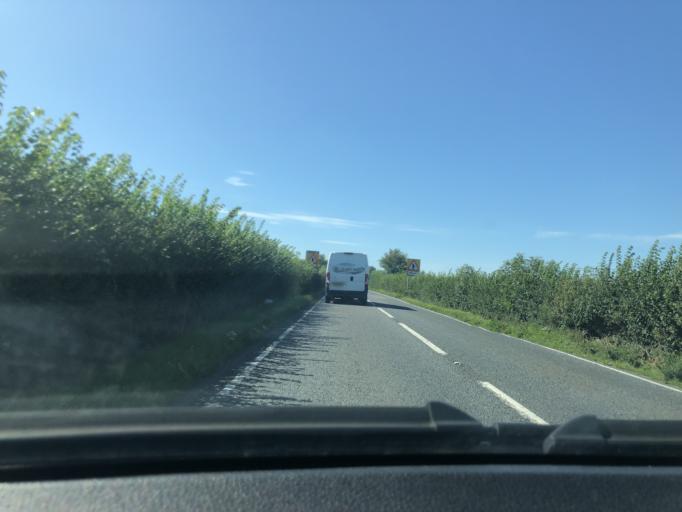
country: GB
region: England
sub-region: Somerset
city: Westonzoyland
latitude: 51.1383
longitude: -2.8664
